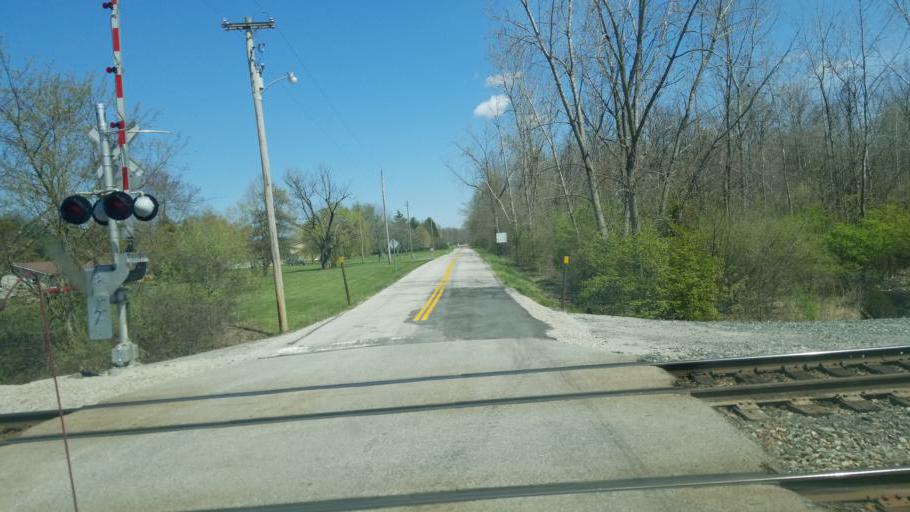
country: US
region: Ohio
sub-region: Delaware County
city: Delaware
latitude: 40.3732
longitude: -83.0824
